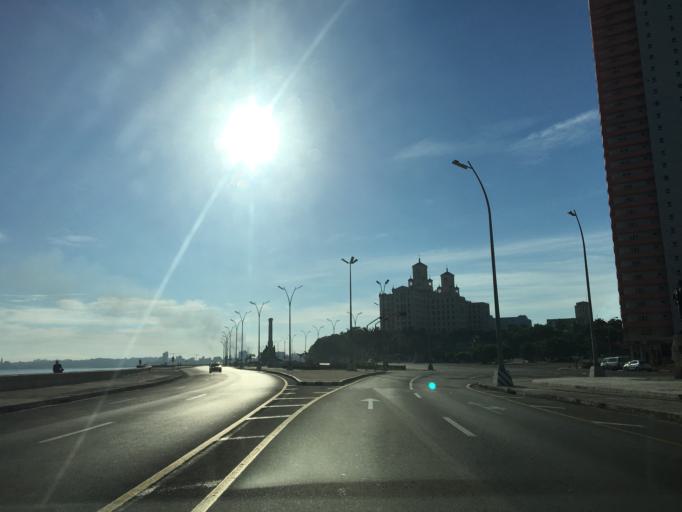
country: CU
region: La Habana
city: Havana
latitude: 23.1454
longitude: -82.3845
